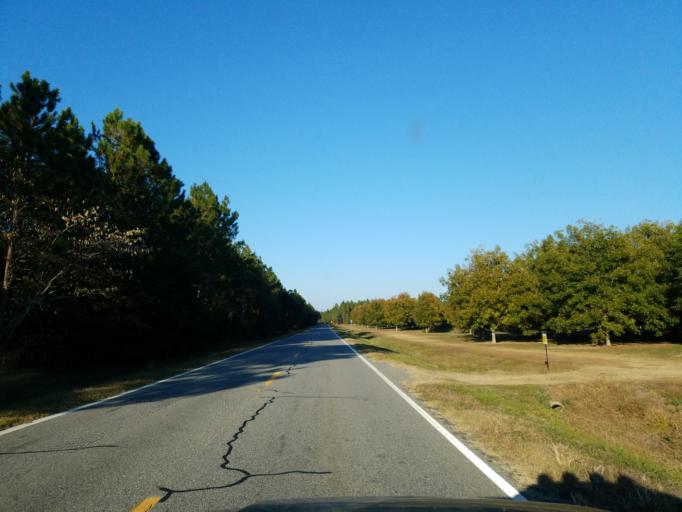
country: US
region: Georgia
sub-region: Lanier County
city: Lakeland
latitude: 30.9773
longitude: -83.0781
